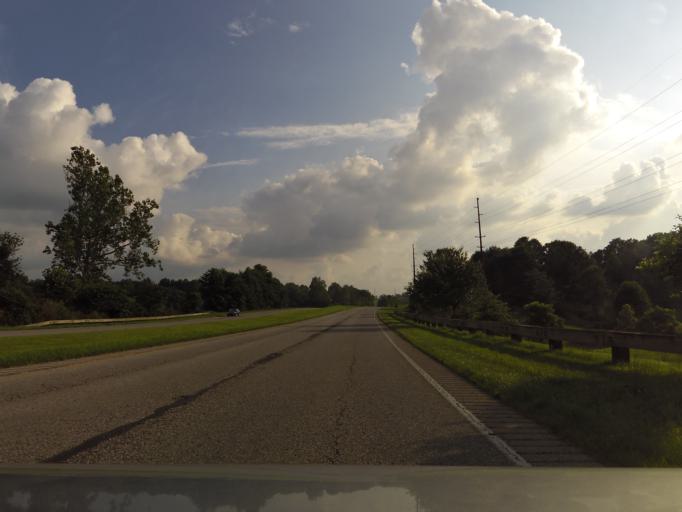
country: US
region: Kentucky
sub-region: Bourbon County
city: Paris
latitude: 38.1588
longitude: -84.3298
